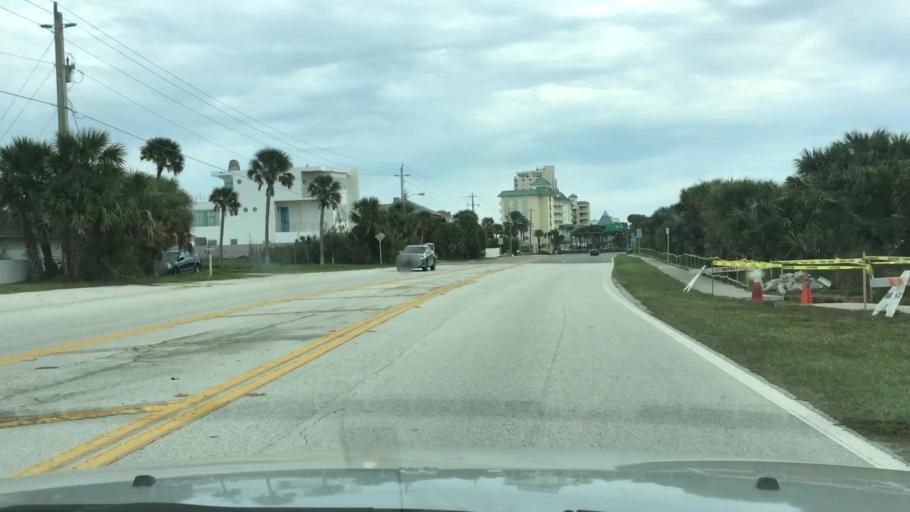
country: US
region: Florida
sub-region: Volusia County
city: Ormond Beach
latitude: 29.2942
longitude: -81.0409
